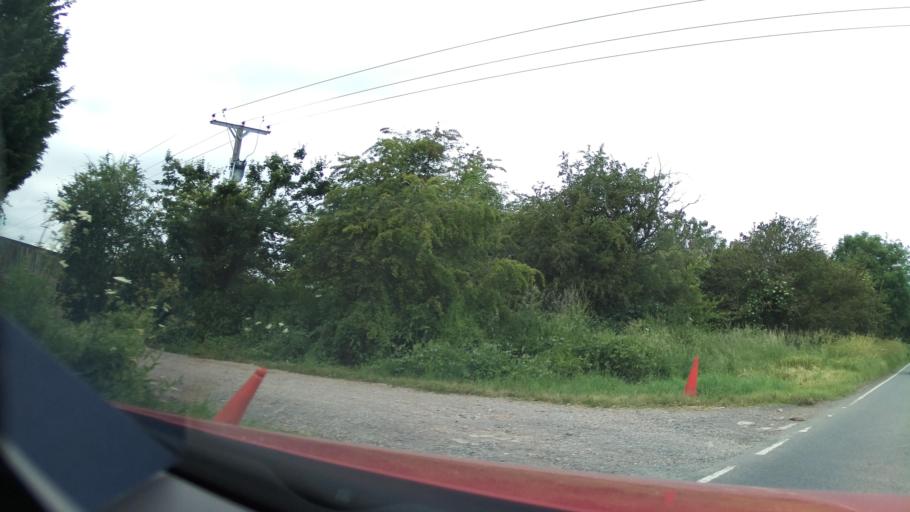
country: GB
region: England
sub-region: Leicestershire
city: Sileby
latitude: 52.8075
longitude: -1.0790
